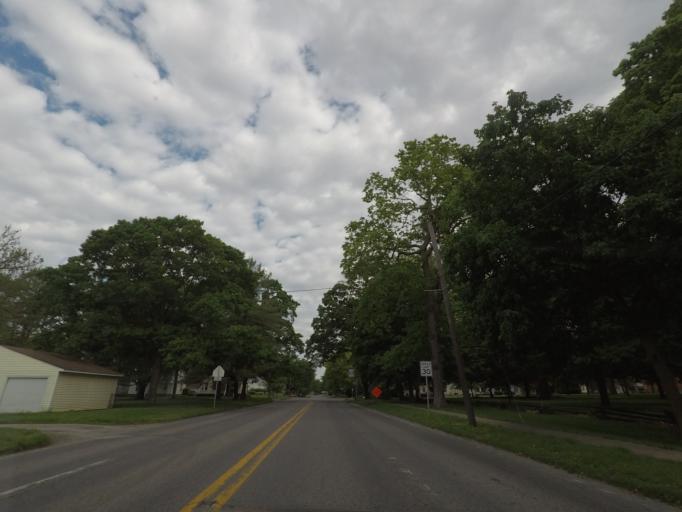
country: US
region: Illinois
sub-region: Logan County
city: Lincoln
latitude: 40.1549
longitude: -89.3622
